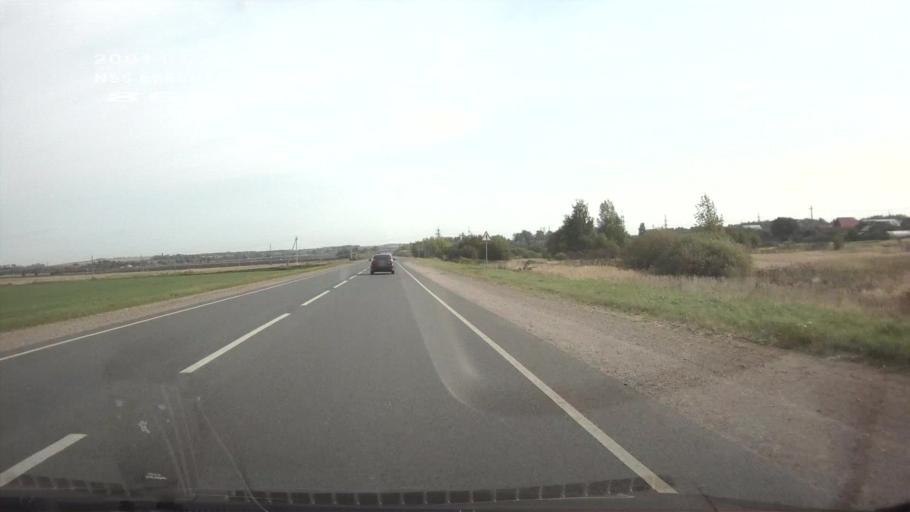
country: RU
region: Mariy-El
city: Yoshkar-Ola
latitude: 56.6688
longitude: 47.9983
